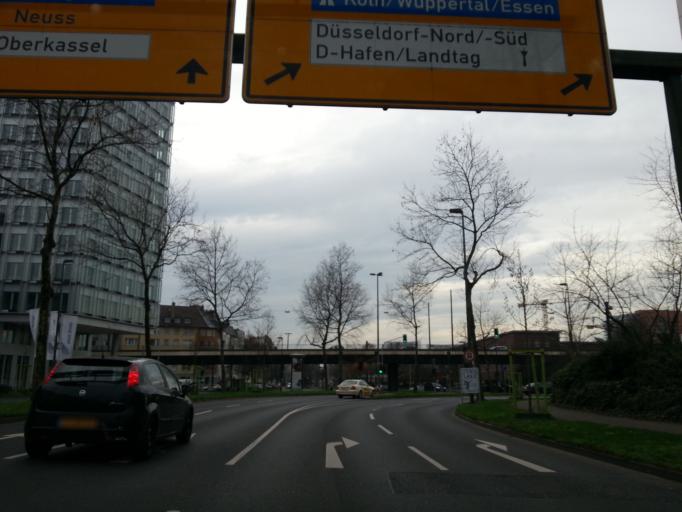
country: DE
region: North Rhine-Westphalia
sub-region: Regierungsbezirk Dusseldorf
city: Dusseldorf
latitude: 51.2181
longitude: 6.7704
